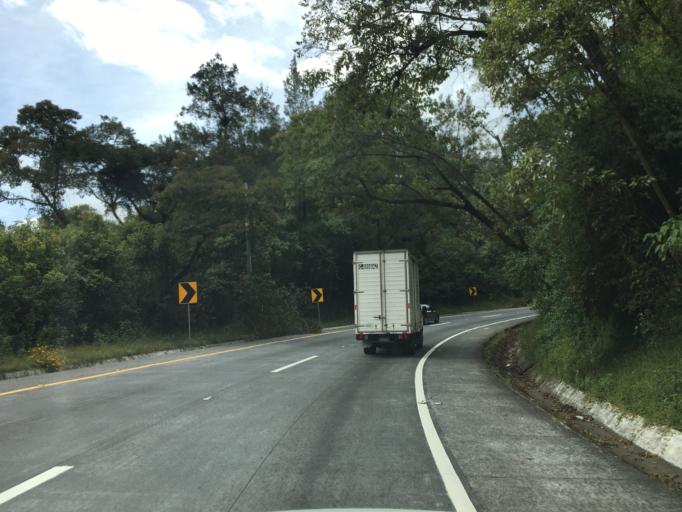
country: GT
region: Sacatepequez
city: Santa Lucia Milpas Altas
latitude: 14.5670
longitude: -90.6859
